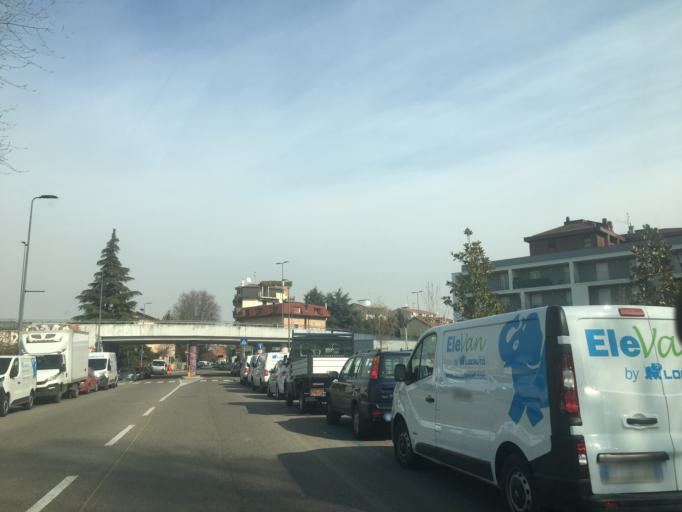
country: IT
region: Lombardy
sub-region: Citta metropolitana di Milano
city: Sesto San Giovanni
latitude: 45.5223
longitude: 9.2226
